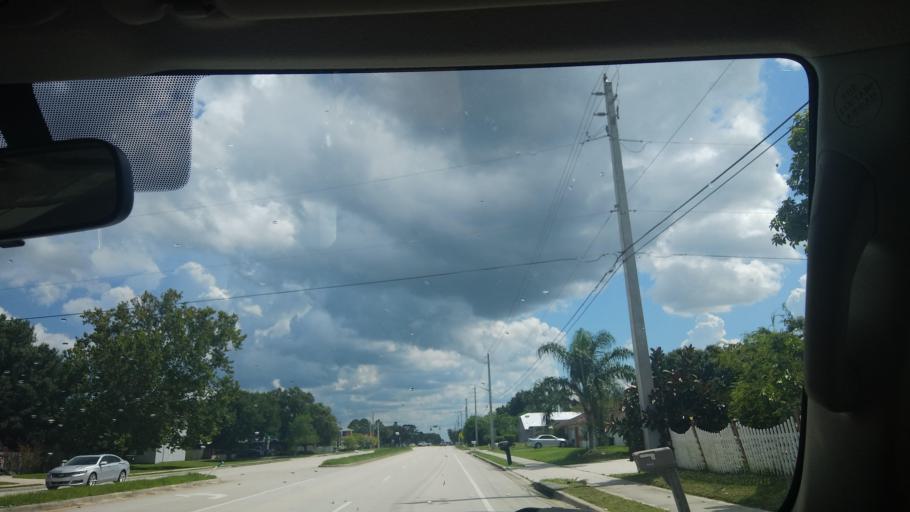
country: US
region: Florida
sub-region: Brevard County
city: Palm Bay
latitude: 27.9895
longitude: -80.6486
